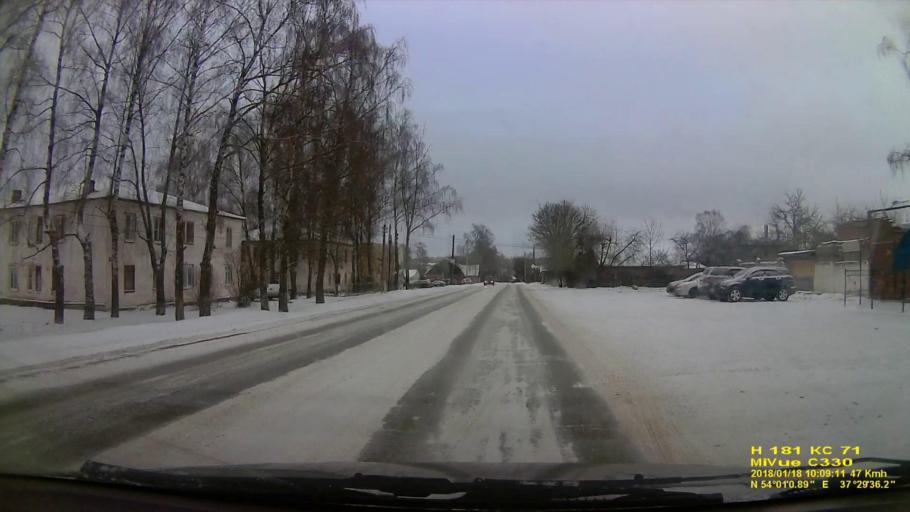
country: RU
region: Tula
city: Shchekino
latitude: 54.0167
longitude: 37.4936
